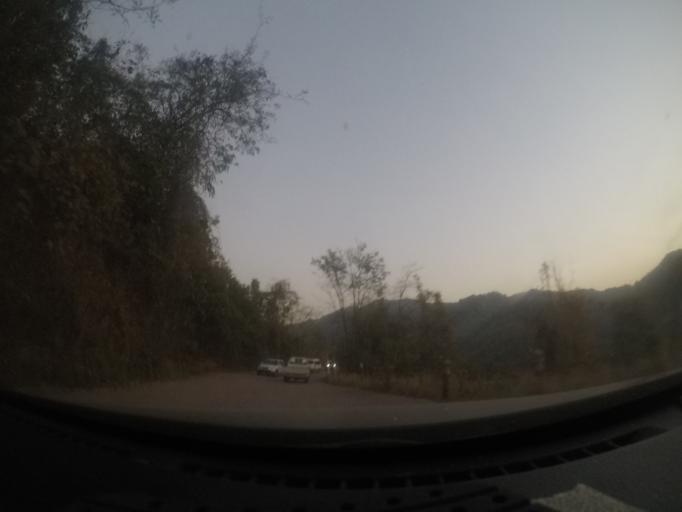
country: MM
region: Mandalay
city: Yamethin
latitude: 20.6959
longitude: 96.5031
